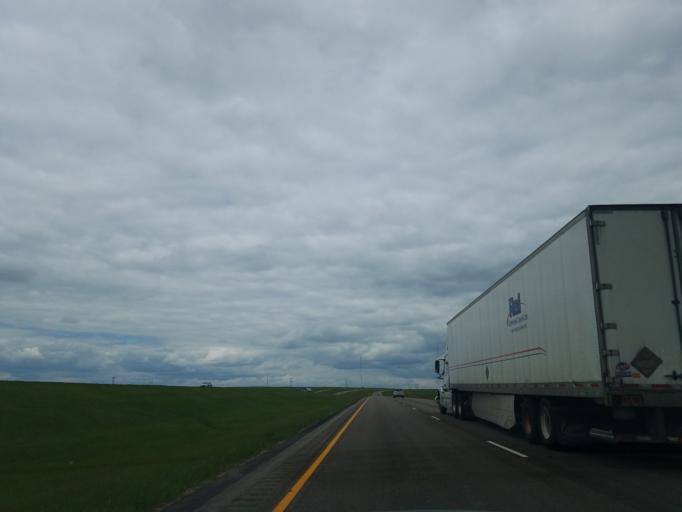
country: US
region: North Dakota
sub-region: Kidder County
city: Steele
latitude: 46.8482
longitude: -100.2415
